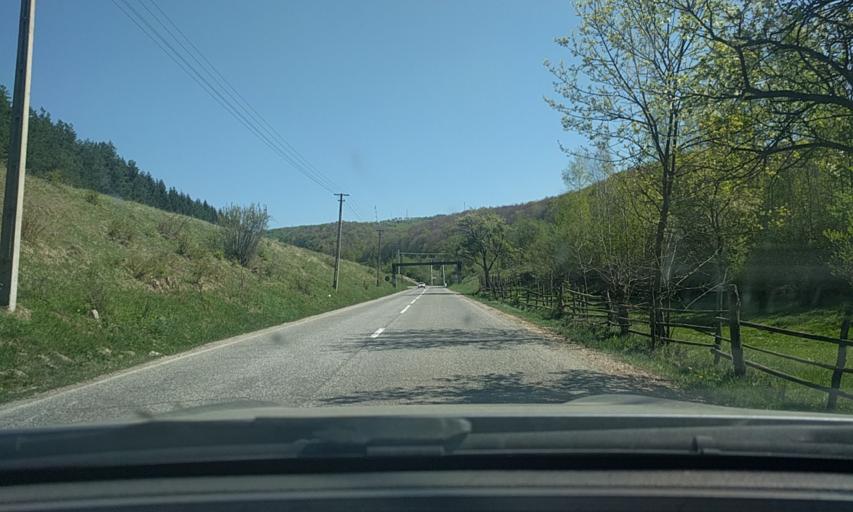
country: RO
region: Brasov
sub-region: Comuna Vama Buzaului
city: Acris
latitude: 45.6798
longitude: 25.9355
